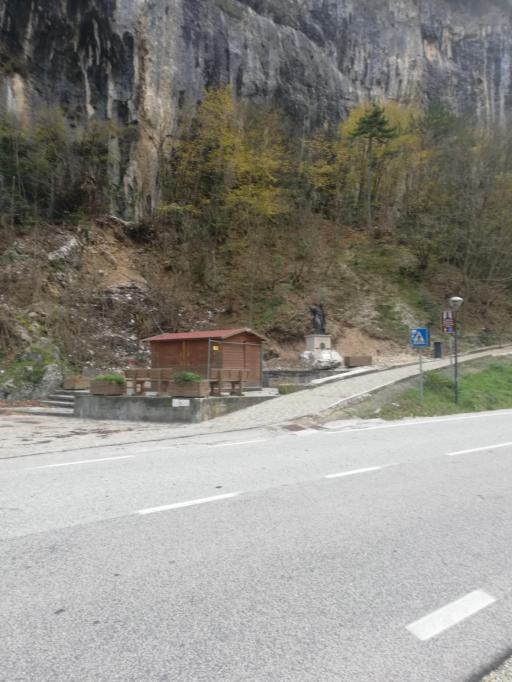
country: IT
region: The Marches
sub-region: Provincia di Ancona
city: Genga
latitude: 43.4050
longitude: 12.9471
